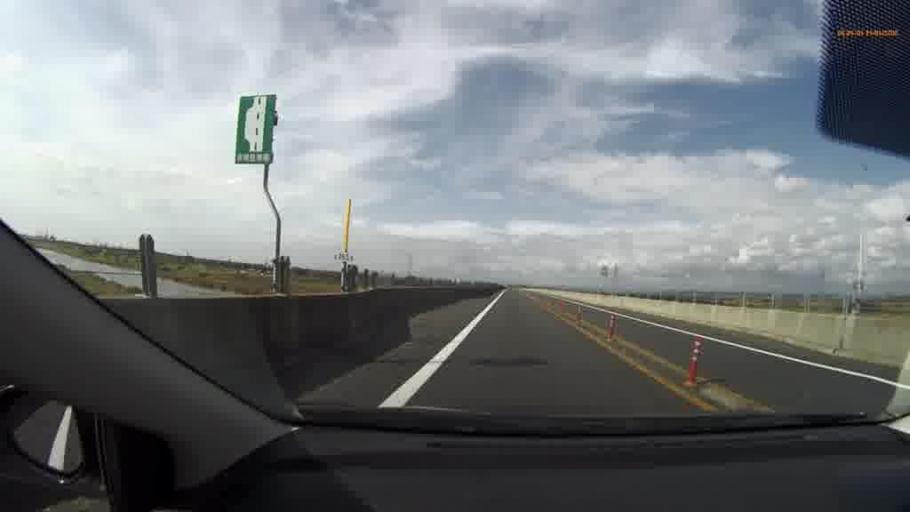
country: JP
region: Hokkaido
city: Kushiro
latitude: 43.0335
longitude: 144.3842
